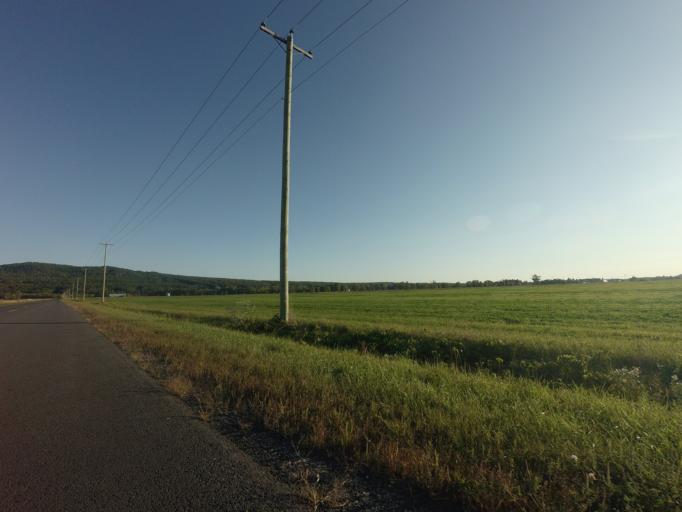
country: CA
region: Quebec
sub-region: Monteregie
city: Rigaud
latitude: 45.4794
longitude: -74.3434
